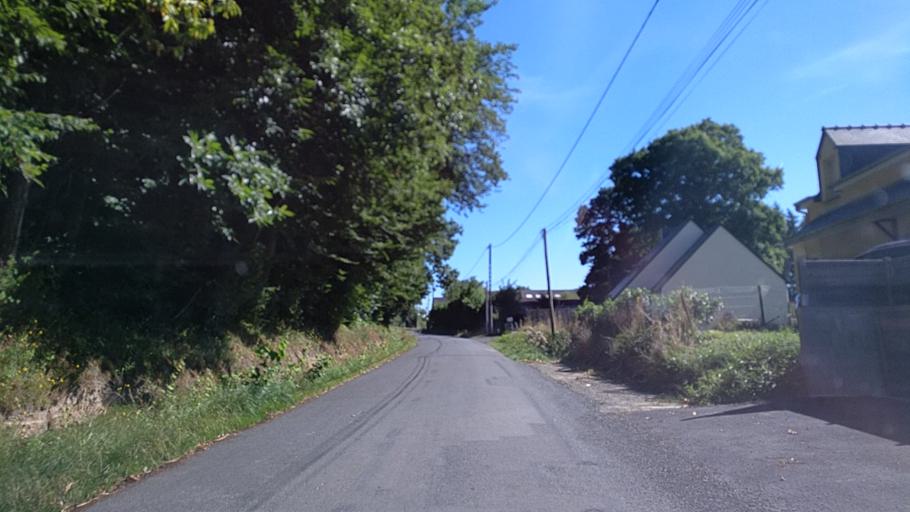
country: FR
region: Brittany
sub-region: Departement d'Ille-et-Vilaine
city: Plerguer
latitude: 48.5267
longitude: -1.8603
